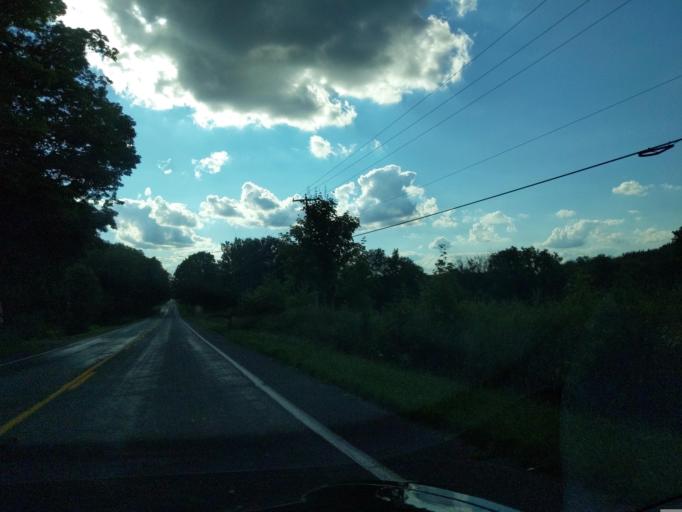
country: US
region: Michigan
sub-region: Ingham County
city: Holt
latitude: 42.5821
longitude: -84.5340
